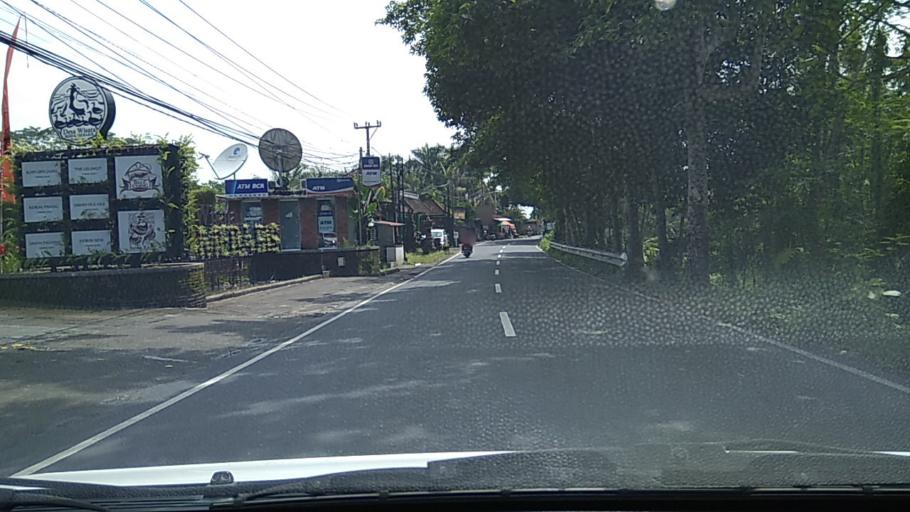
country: ID
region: Bali
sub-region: Kabupaten Gianyar
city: Ubud
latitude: -8.5228
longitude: 115.2795
